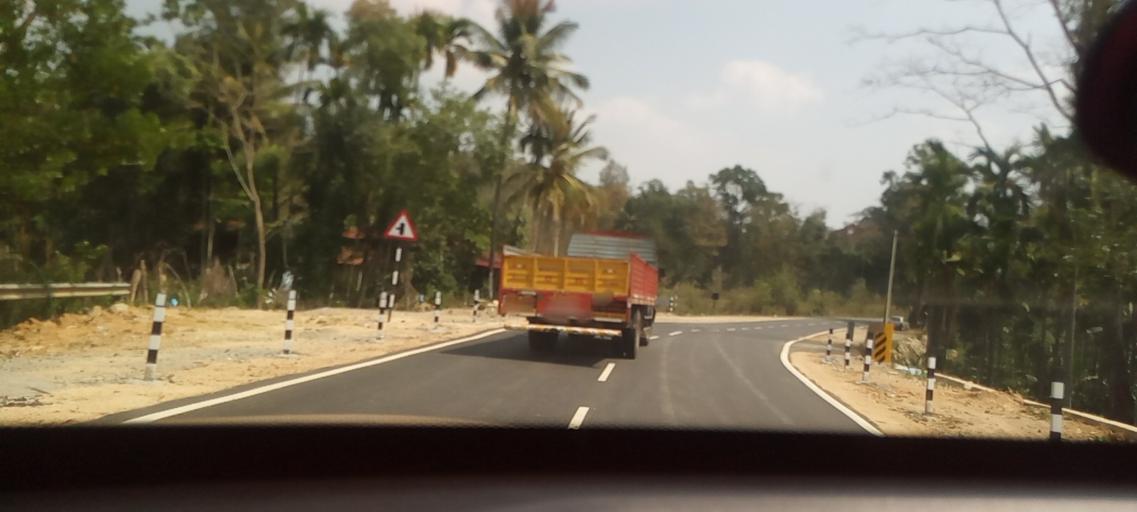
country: IN
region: Karnataka
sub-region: Chikmagalur
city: Mudigere
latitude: 13.3138
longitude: 75.5741
